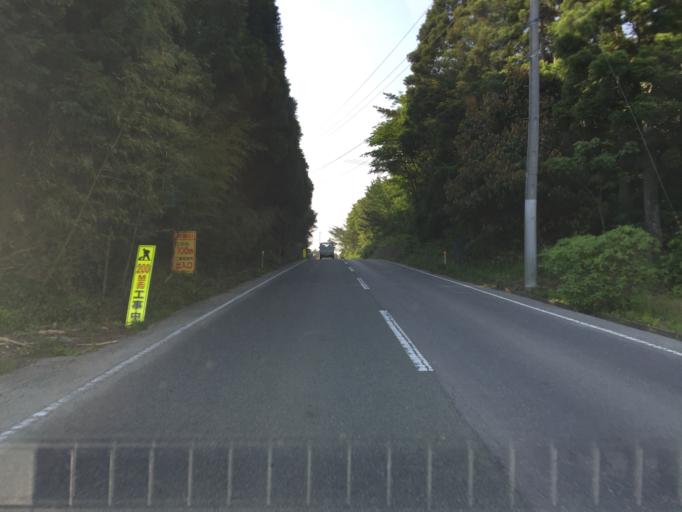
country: JP
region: Fukushima
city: Namie
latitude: 37.7416
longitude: 141.0052
